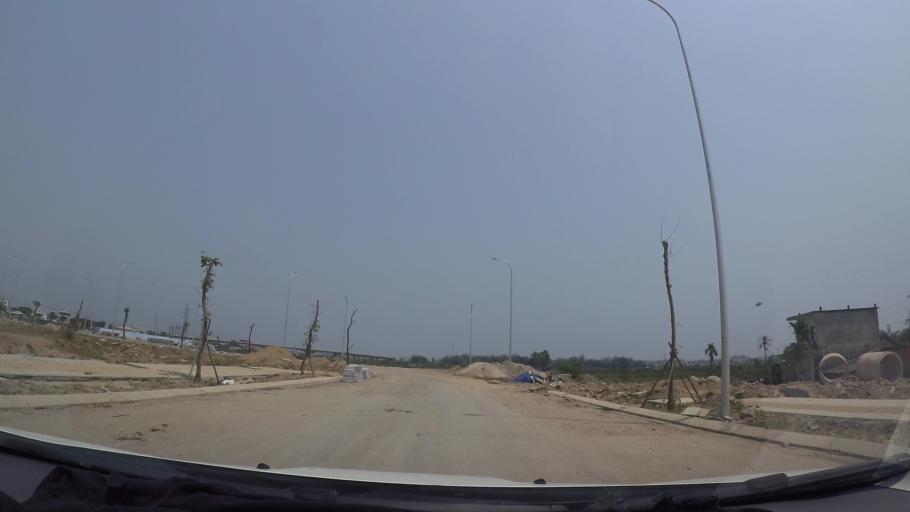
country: VN
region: Da Nang
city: Cam Le
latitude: 15.9983
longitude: 108.2243
